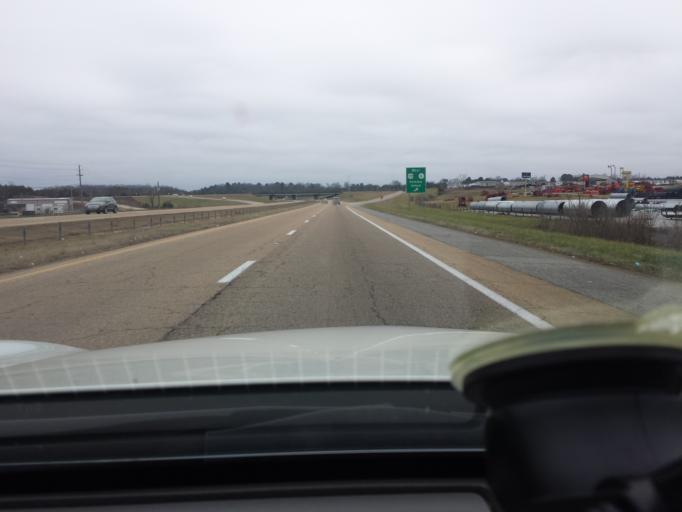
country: US
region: Mississippi
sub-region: Lee County
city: Verona
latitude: 34.2151
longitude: -88.7063
